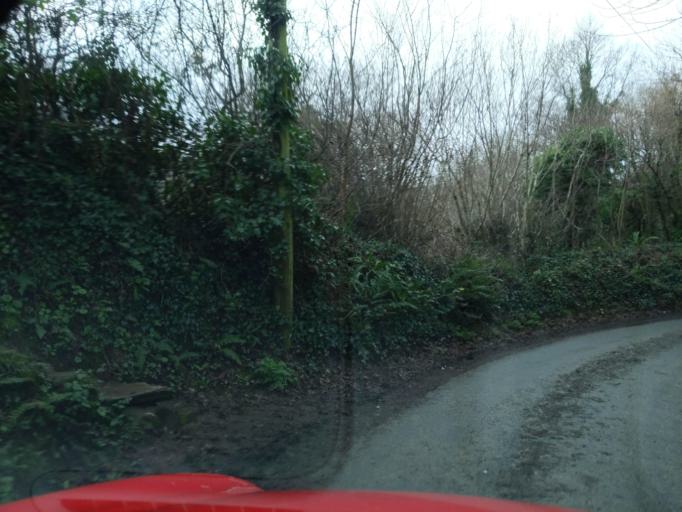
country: GB
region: England
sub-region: Cornwall
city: Fowey
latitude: 50.3377
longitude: -4.5812
